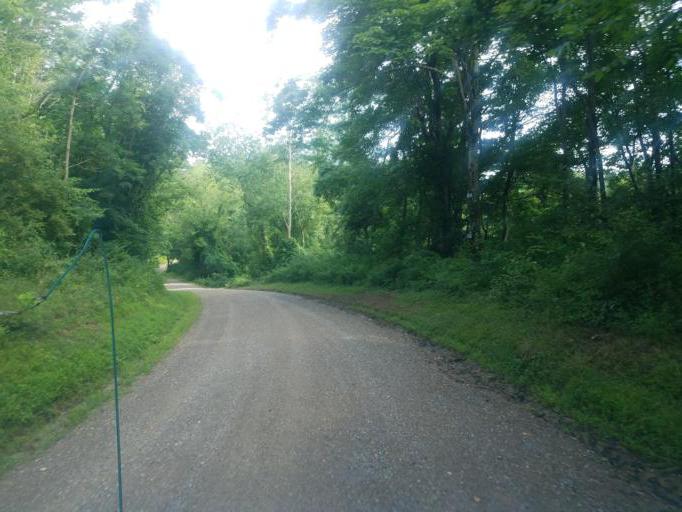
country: US
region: Ohio
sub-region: Knox County
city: Oak Hill
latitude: 40.3843
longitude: -82.1667
